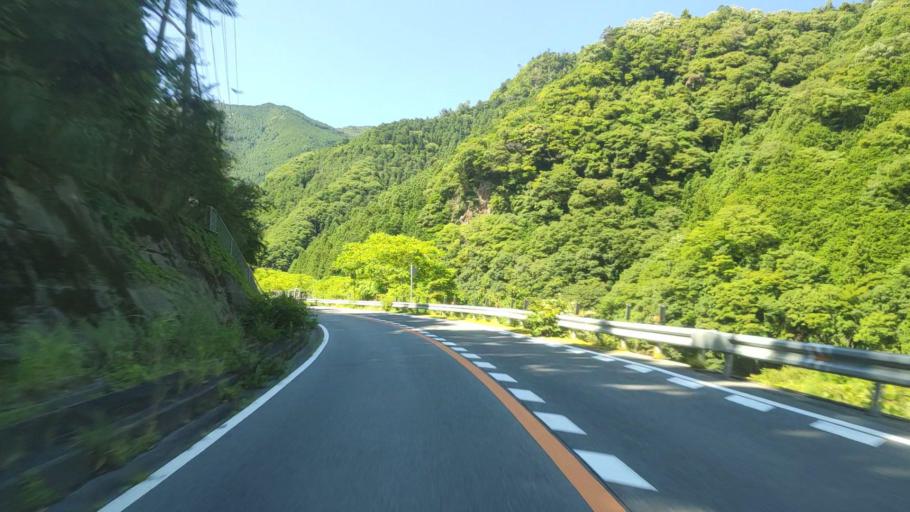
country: JP
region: Nara
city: Yoshino-cho
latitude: 34.3104
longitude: 135.9929
